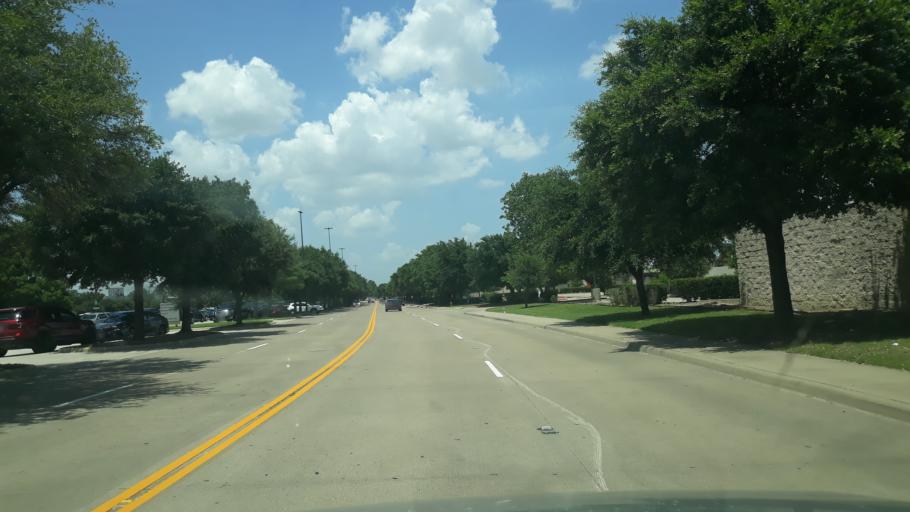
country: US
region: Texas
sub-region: Dallas County
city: Coppell
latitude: 32.9648
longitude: -97.0395
